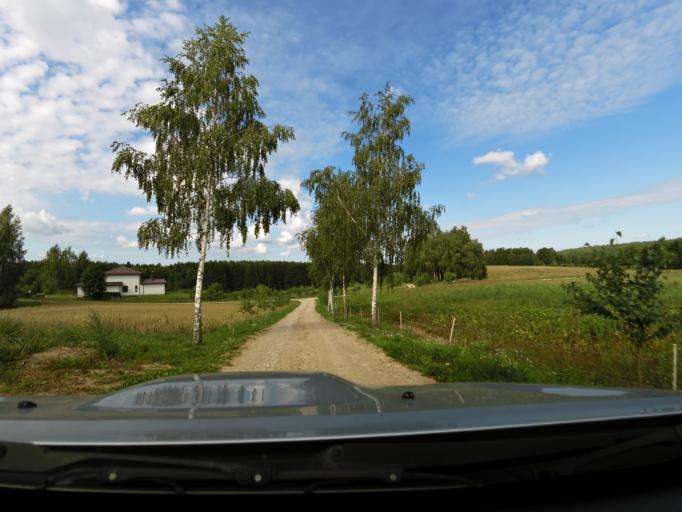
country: LT
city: Grigiskes
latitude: 54.7786
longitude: 25.0124
